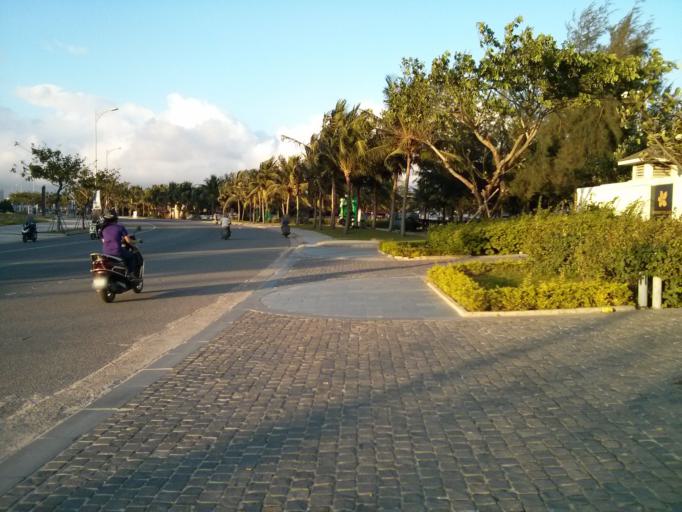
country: VN
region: Da Nang
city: Son Tra
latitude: 16.0459
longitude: 108.2495
